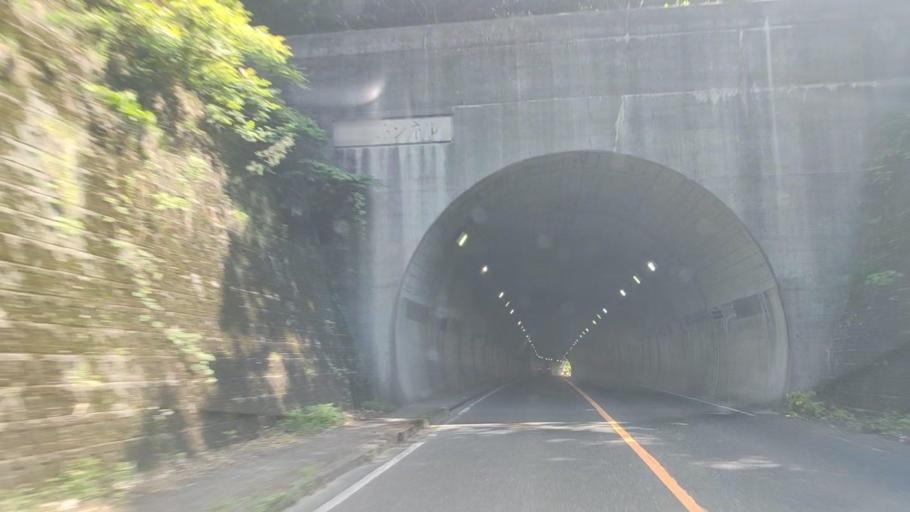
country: JP
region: Tottori
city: Tottori
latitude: 35.5327
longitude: 134.2300
